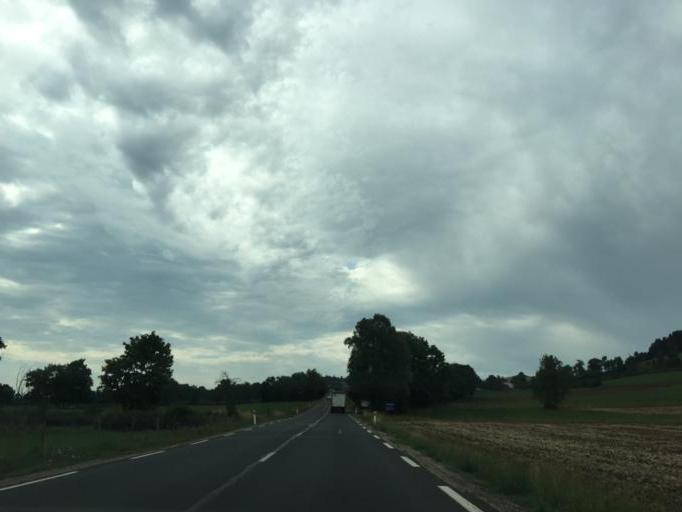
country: FR
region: Auvergne
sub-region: Departement de la Haute-Loire
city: Solignac-sur-Loire
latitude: 44.9508
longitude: 3.8456
